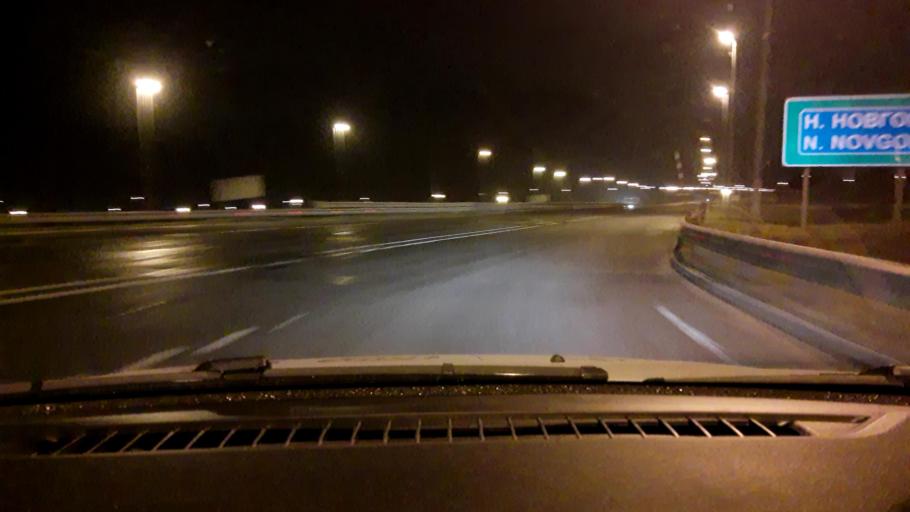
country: RU
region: Nizjnij Novgorod
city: Burevestnik
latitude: 56.1166
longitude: 43.9145
